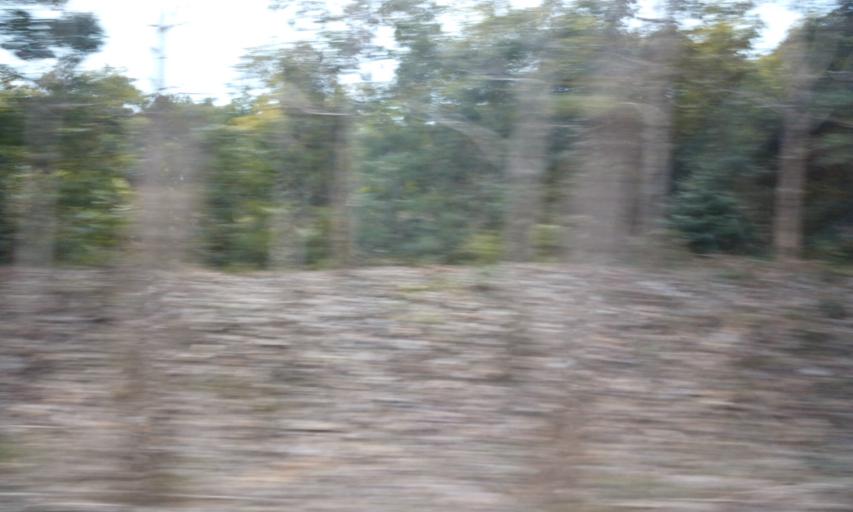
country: TH
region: Phayao
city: Phu Sang
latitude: 19.5999
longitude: 100.3226
